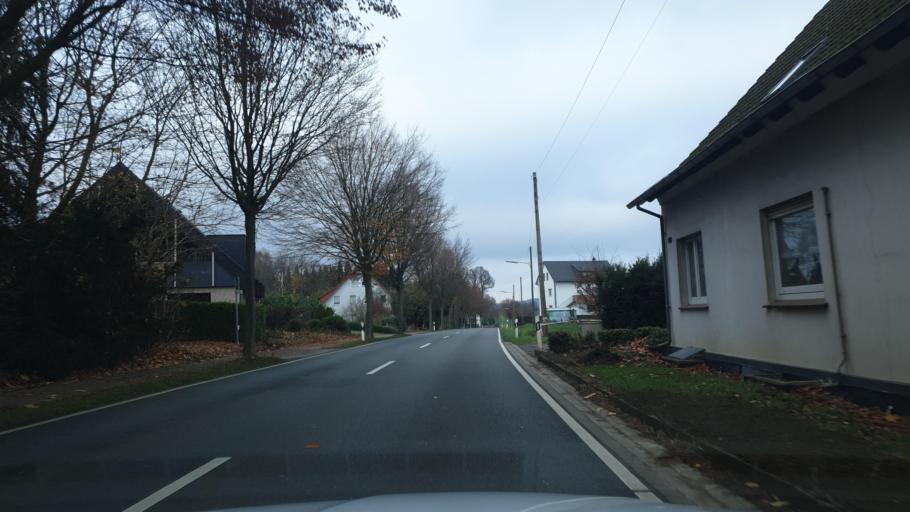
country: DE
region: North Rhine-Westphalia
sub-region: Regierungsbezirk Detmold
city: Hiddenhausen
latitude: 52.1520
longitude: 8.6225
